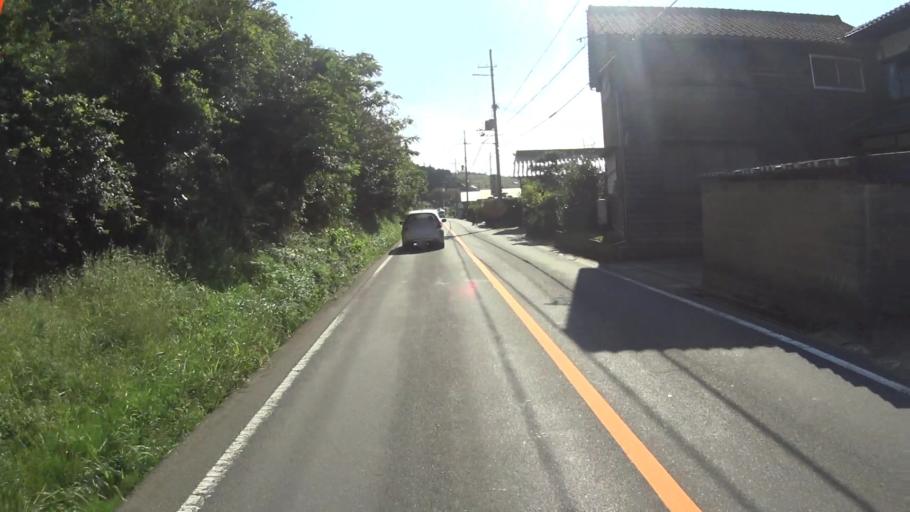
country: JP
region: Kyoto
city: Miyazu
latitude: 35.7002
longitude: 135.0614
